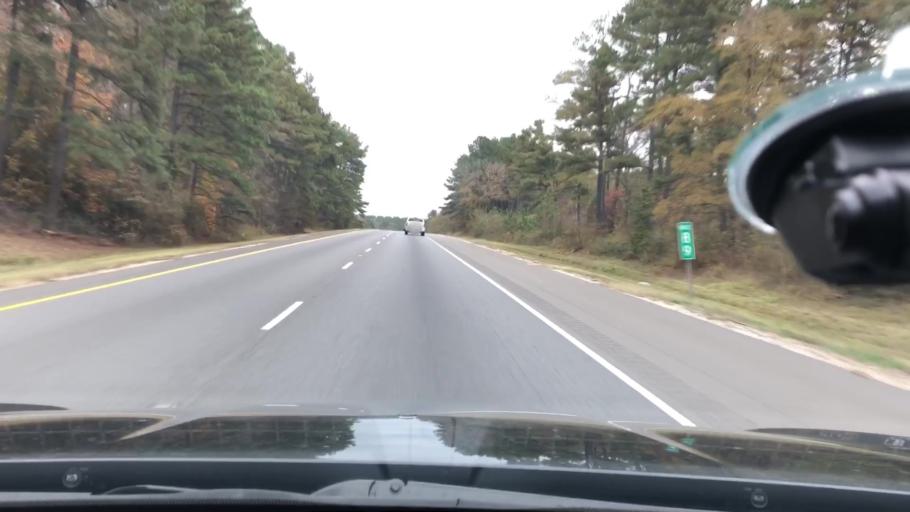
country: US
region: Arkansas
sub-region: Hot Spring County
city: Malvern
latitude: 34.3098
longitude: -92.9391
